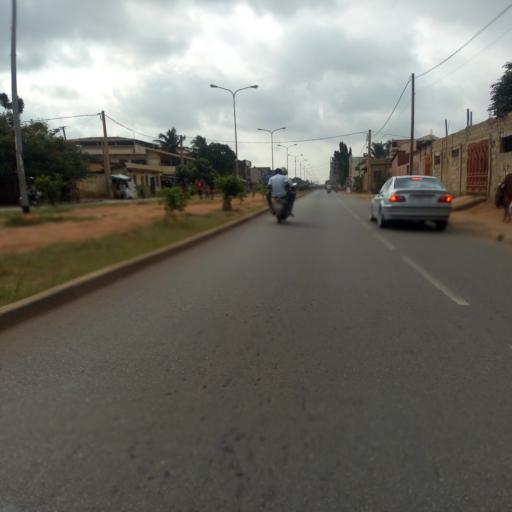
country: TG
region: Maritime
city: Lome
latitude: 6.1942
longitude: 1.2401
